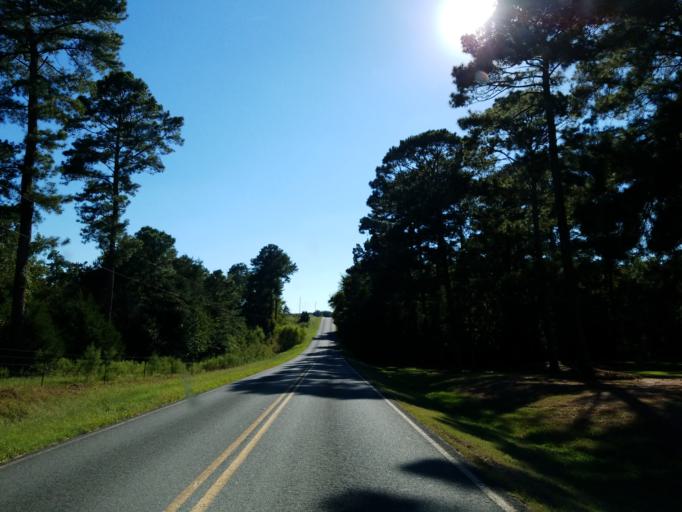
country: US
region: Georgia
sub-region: Dooly County
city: Unadilla
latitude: 32.2514
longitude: -83.7911
